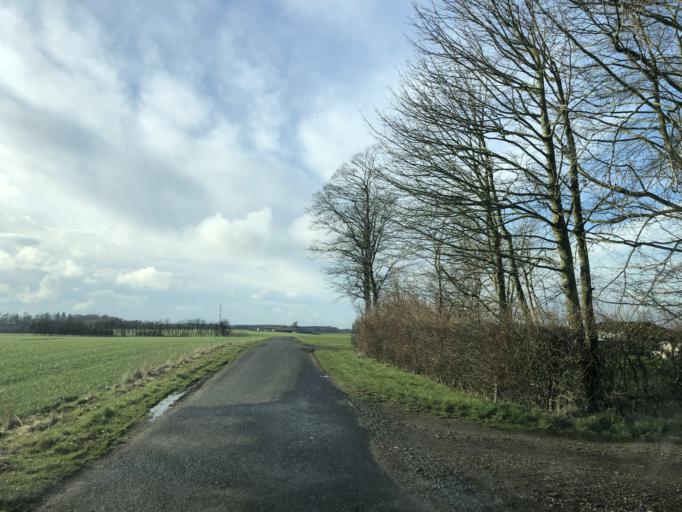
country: DK
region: North Denmark
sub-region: Vesthimmerland Kommune
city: Alestrup
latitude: 56.6441
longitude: 9.6306
